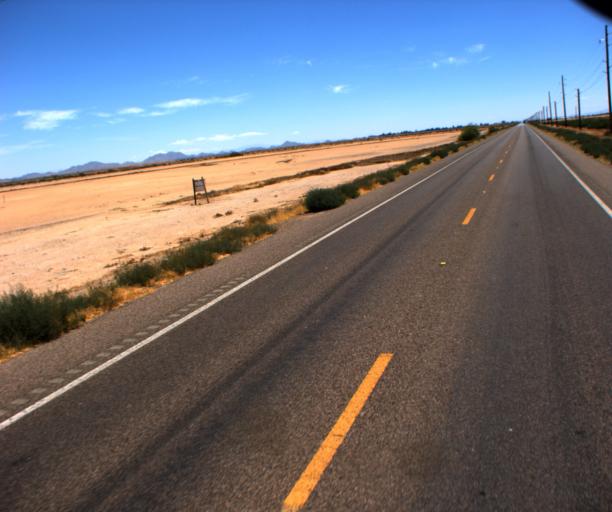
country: US
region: Arizona
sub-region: Pinal County
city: Casa Grande
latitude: 32.8794
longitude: -111.9087
